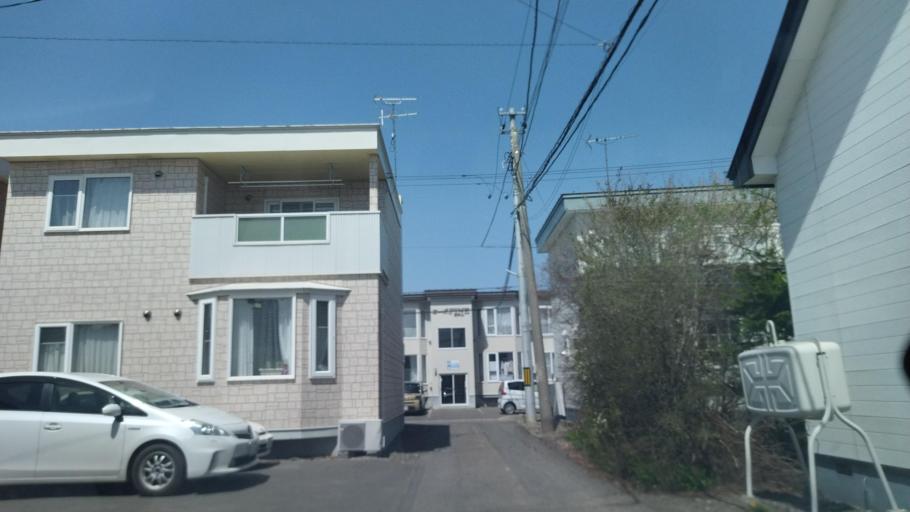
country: JP
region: Hokkaido
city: Obihiro
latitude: 42.9321
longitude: 143.1740
